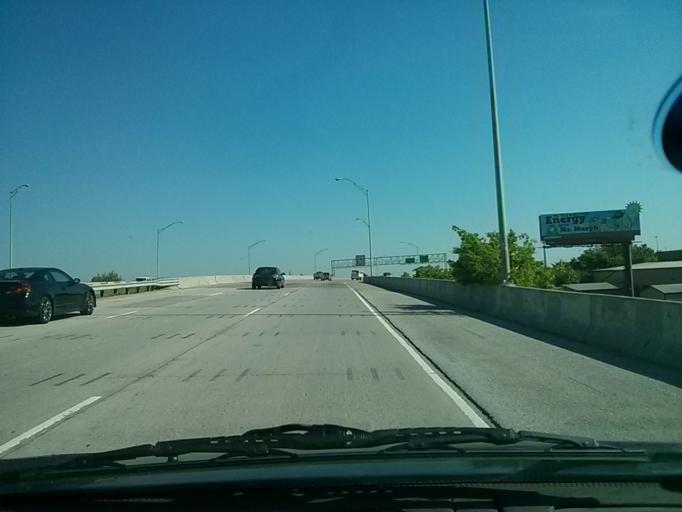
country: US
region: Oklahoma
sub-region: Tulsa County
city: Tulsa
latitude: 36.1702
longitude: -95.9799
